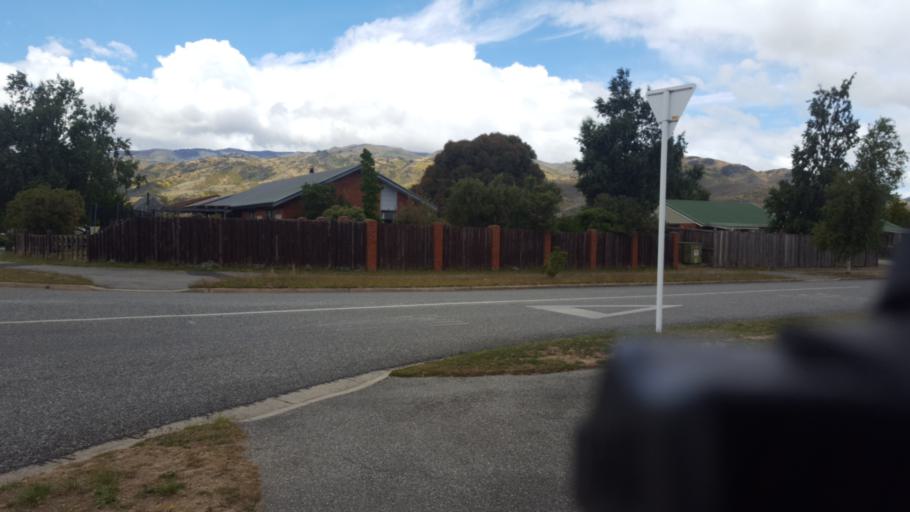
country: NZ
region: Otago
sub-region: Queenstown-Lakes District
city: Wanaka
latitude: -45.0385
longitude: 169.1925
